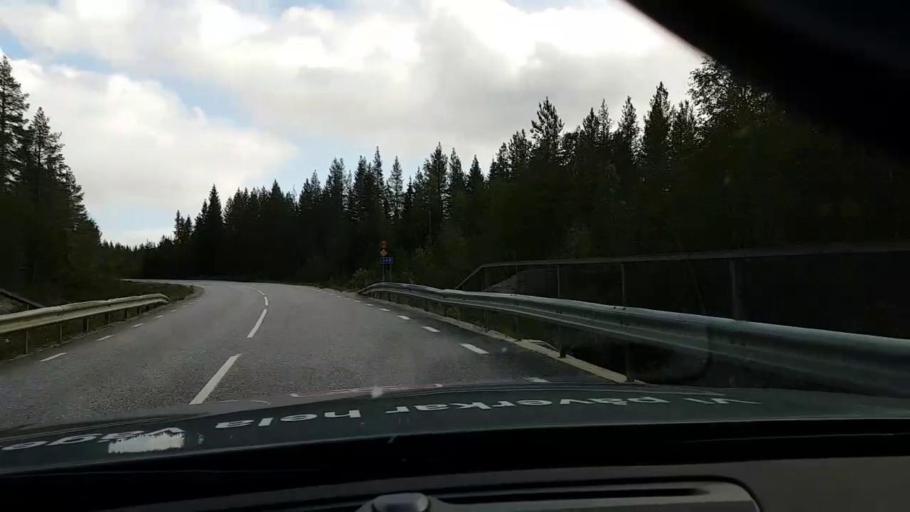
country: SE
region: Vaesternorrland
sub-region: OErnskoeldsviks Kommun
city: Bredbyn
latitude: 63.6867
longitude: 17.7711
